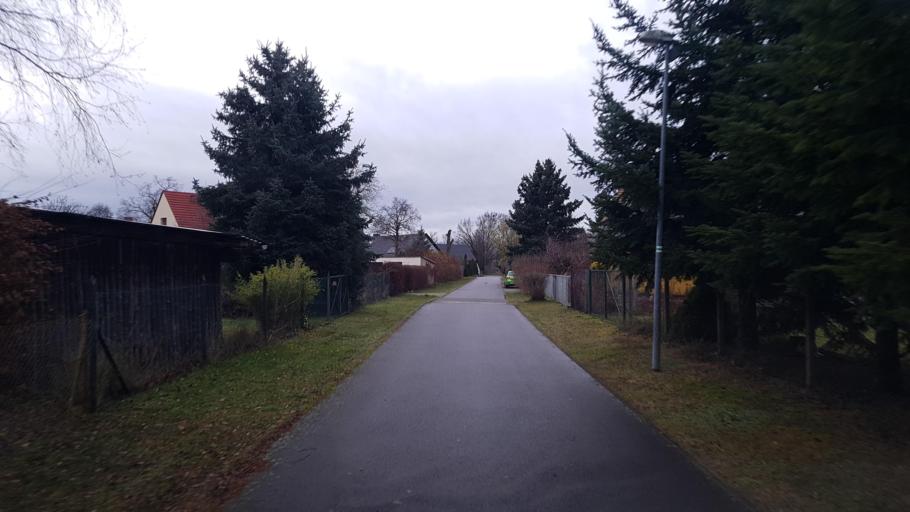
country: DE
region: Brandenburg
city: Luebben
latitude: 51.9461
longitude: 13.9151
